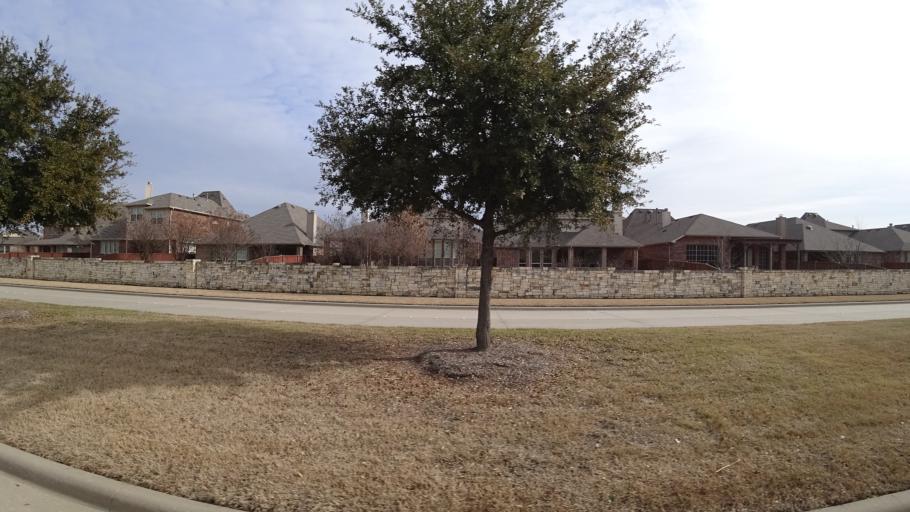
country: US
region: Texas
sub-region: Denton County
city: The Colony
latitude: 33.0544
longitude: -96.9072
